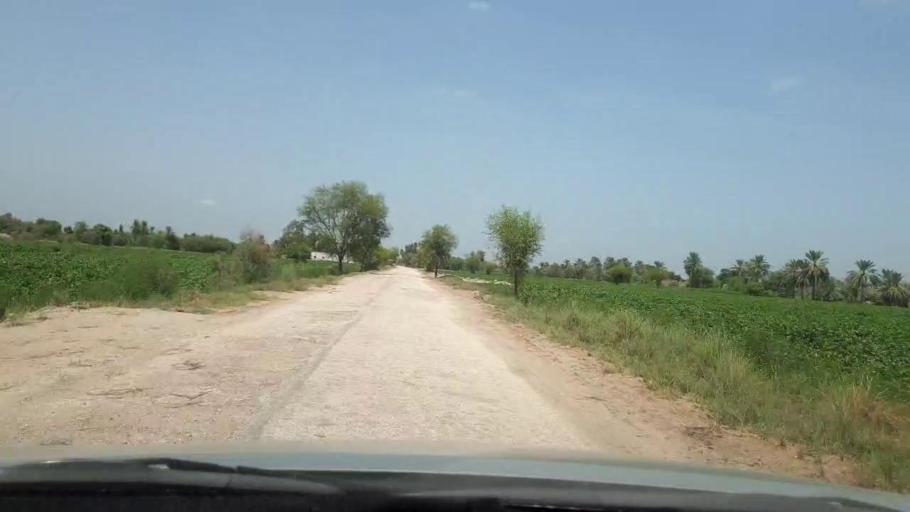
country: PK
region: Sindh
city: Pano Aqil
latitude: 27.7053
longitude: 69.2175
